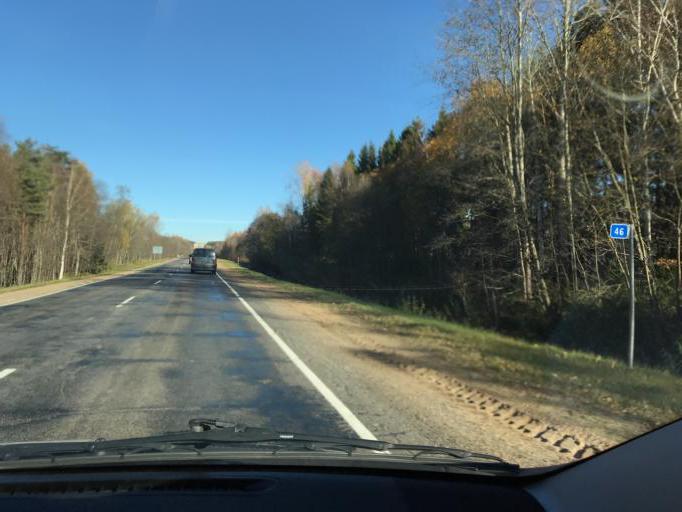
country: BY
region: Vitebsk
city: Polatsk
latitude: 55.3269
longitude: 28.7841
